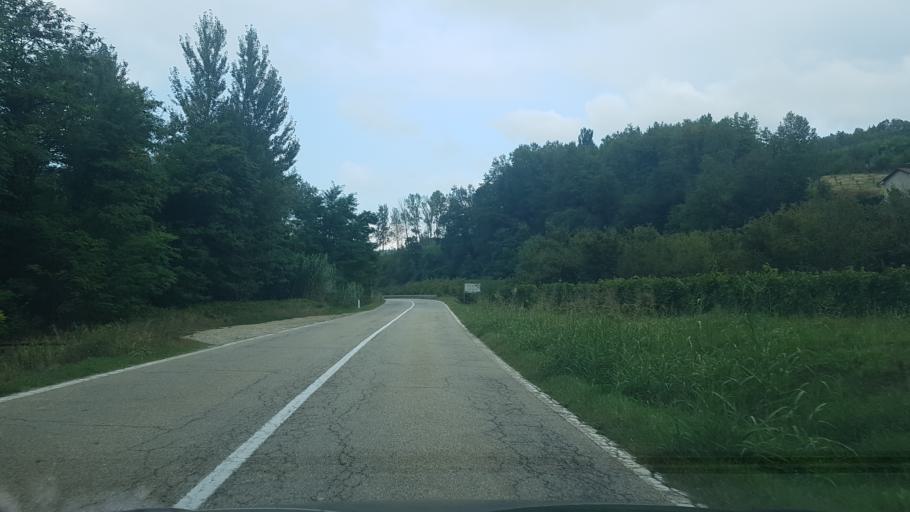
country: IT
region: Piedmont
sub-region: Provincia di Cuneo
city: Cossano Belbo
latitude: 44.6564
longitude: 8.1908
